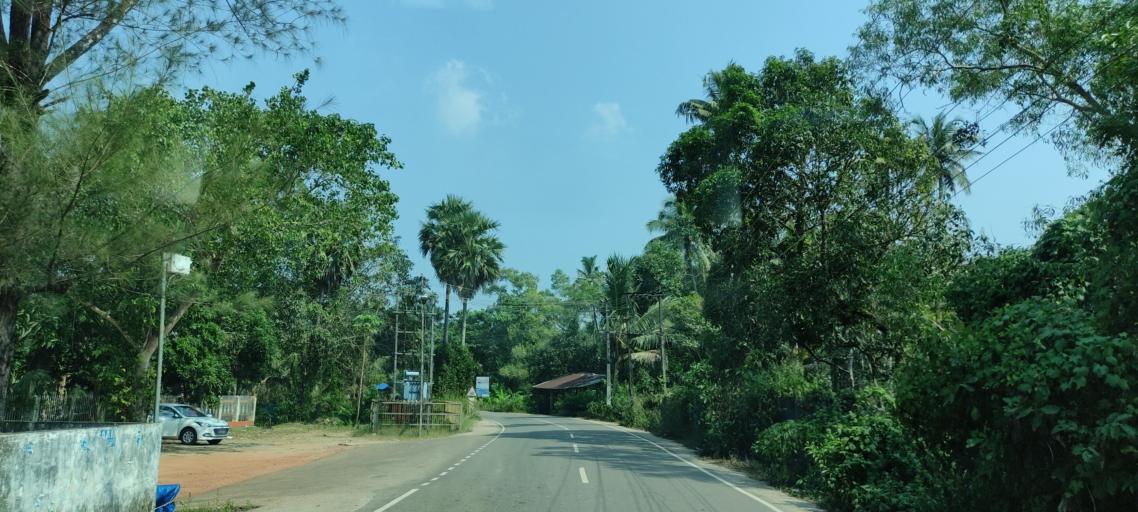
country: IN
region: Kerala
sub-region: Alappuzha
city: Shertallai
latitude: 9.6011
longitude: 76.3165
